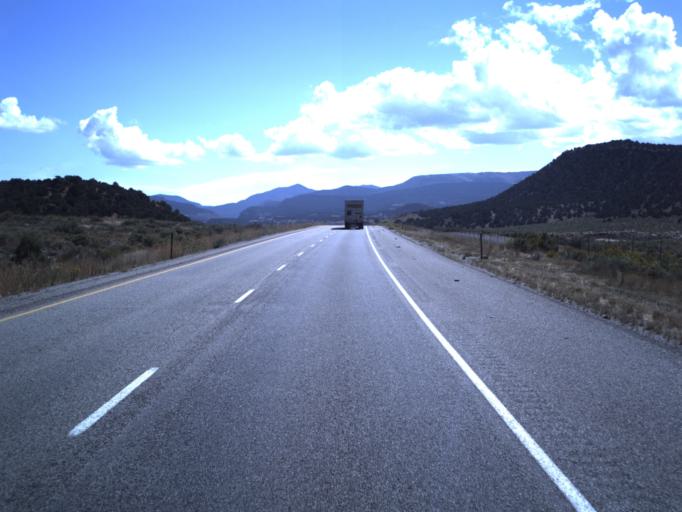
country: US
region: Utah
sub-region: Sevier County
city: Salina
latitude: 38.9235
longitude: -111.7695
